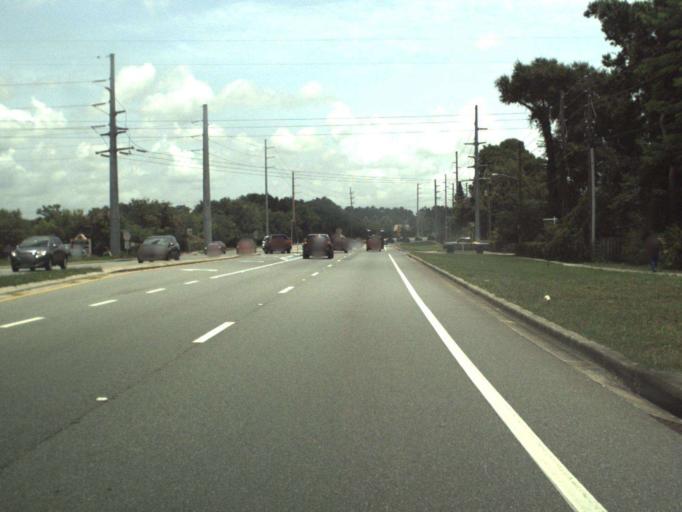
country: US
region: Florida
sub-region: Seminole County
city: Goldenrod
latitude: 28.6163
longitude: -81.2707
